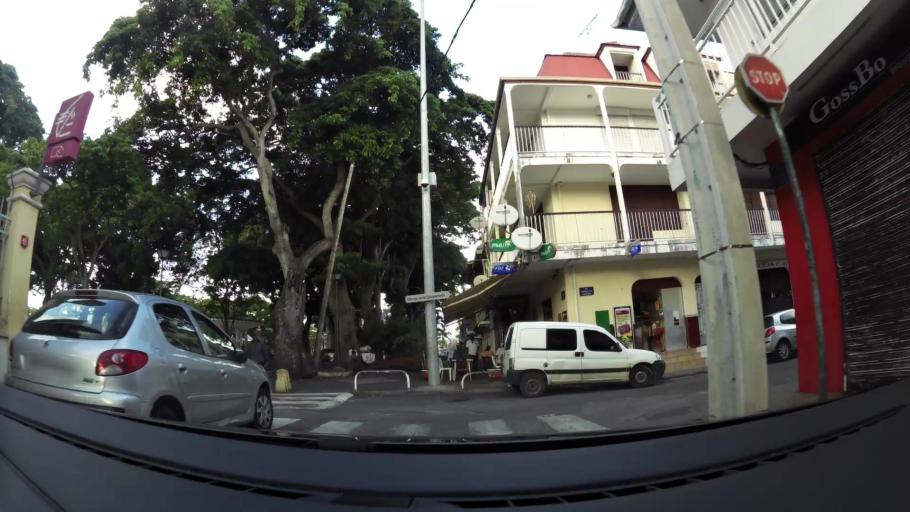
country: GP
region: Guadeloupe
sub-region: Guadeloupe
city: Pointe-a-Pitre
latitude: 16.2379
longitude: -61.5331
